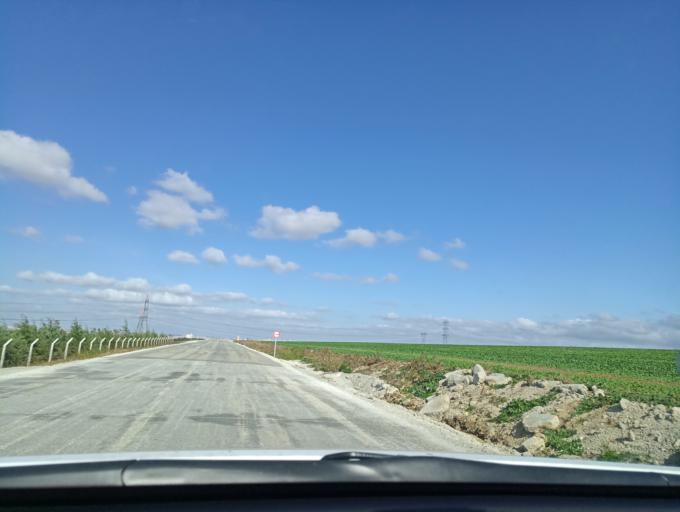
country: TR
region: Tekirdag
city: Corlu
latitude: 41.0549
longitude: 27.8350
